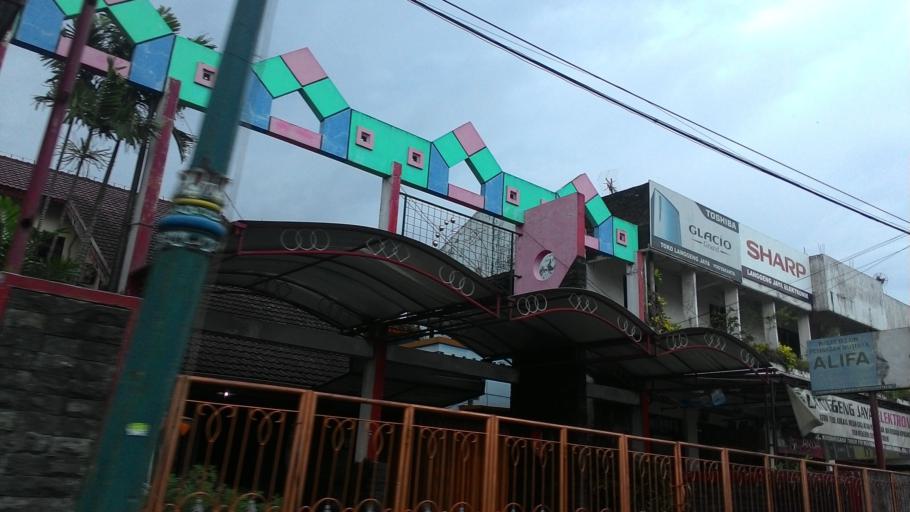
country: ID
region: Daerah Istimewa Yogyakarta
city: Yogyakarta
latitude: -7.8023
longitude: 110.4013
